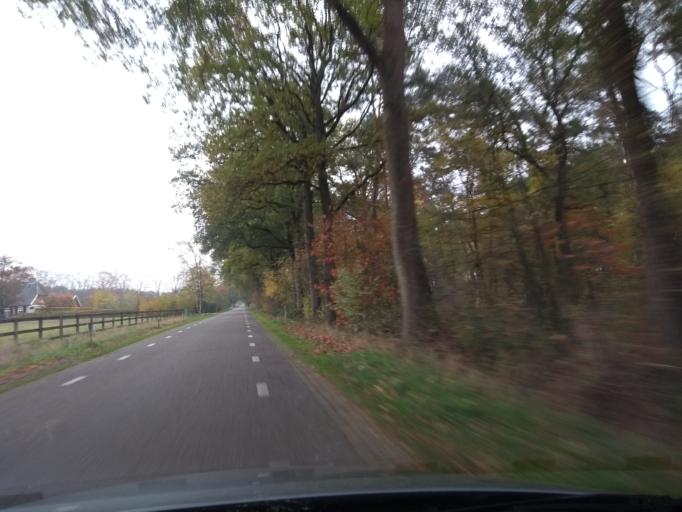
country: NL
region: Gelderland
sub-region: Gemeente Bronckhorst
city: Hengelo
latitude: 52.0379
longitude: 6.3372
